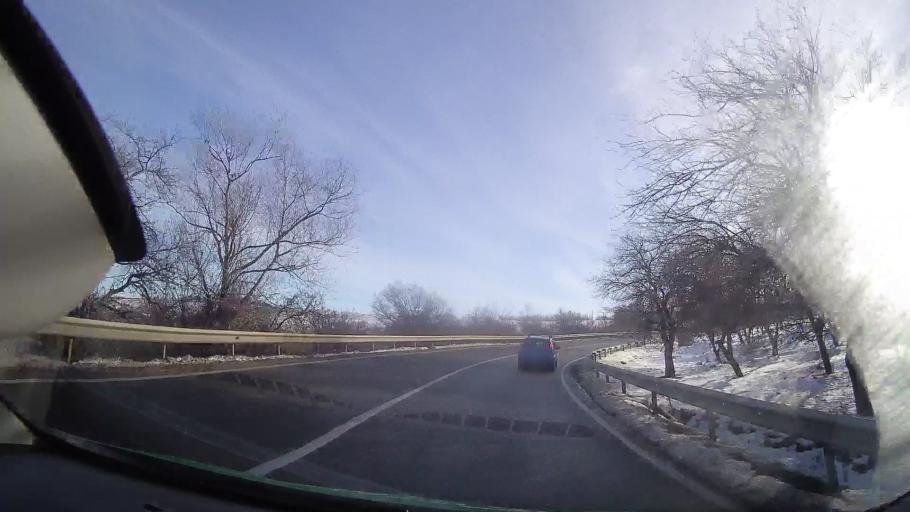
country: RO
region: Neamt
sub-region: Comuna Cracaoani
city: Cracaoani
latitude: 47.1058
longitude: 26.3075
